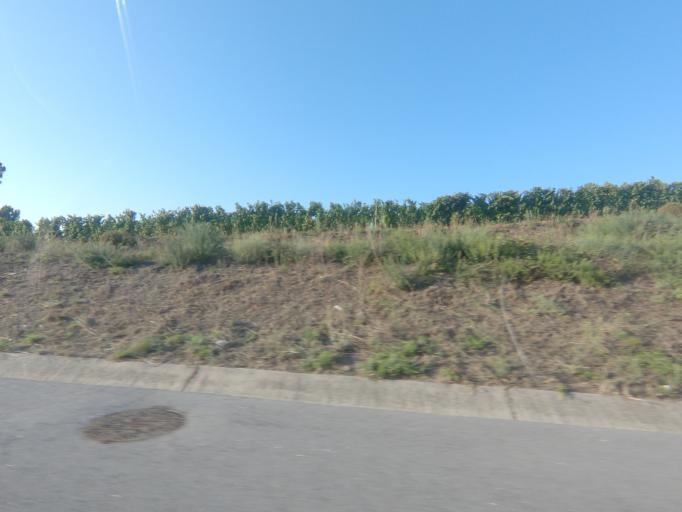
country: PT
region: Vila Real
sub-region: Sabrosa
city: Vilela
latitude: 41.2646
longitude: -7.6290
